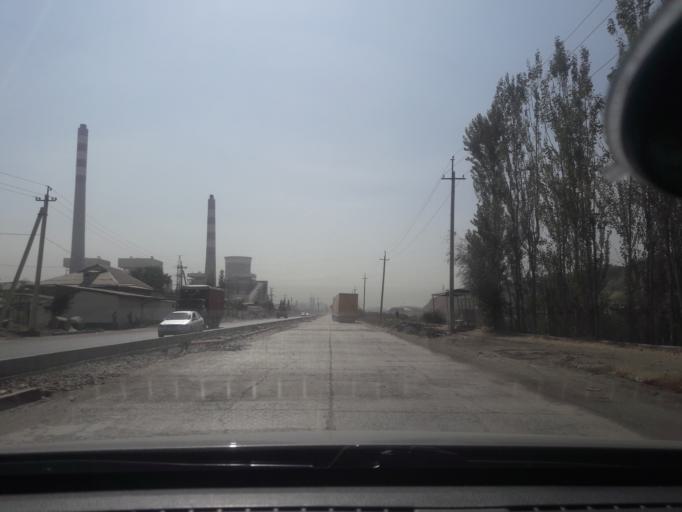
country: TJ
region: Dushanbe
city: Dushanbe
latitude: 38.6154
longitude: 68.7688
